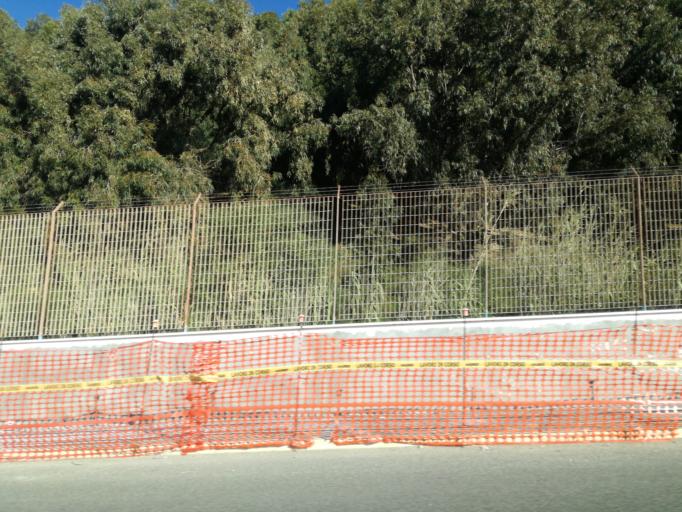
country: IT
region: Sicily
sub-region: Provincia di Caltanissetta
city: Gela
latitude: 37.0693
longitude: 14.2237
